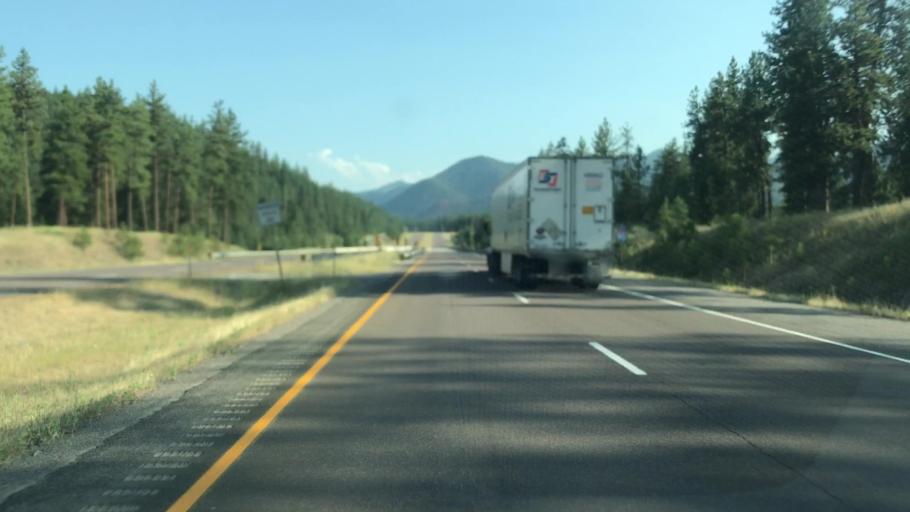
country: US
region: Montana
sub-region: Mineral County
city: Superior
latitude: 47.0711
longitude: -114.7653
